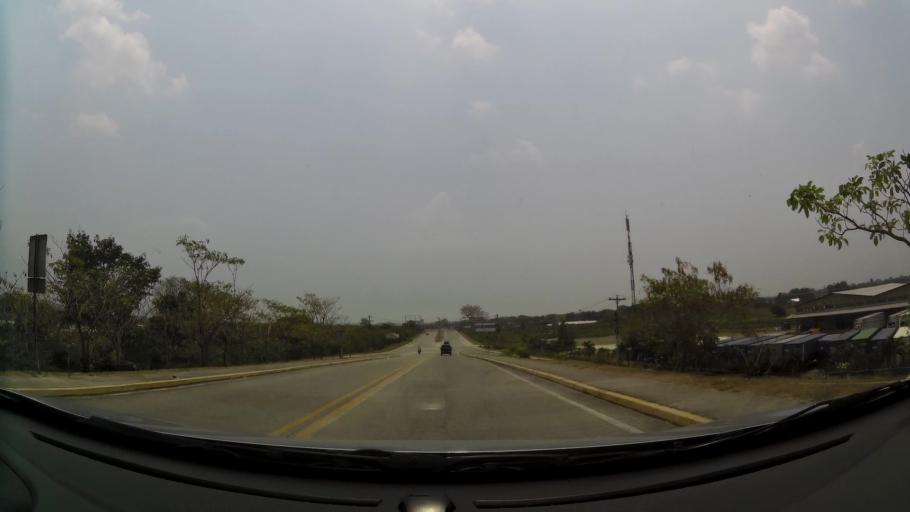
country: HN
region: Cortes
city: La Lima
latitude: 15.4453
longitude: -87.9418
